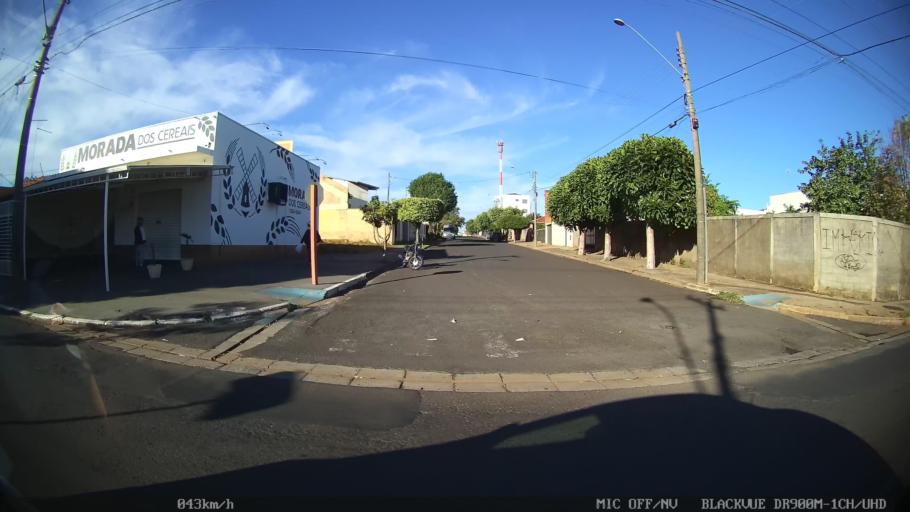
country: BR
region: Sao Paulo
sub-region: Araraquara
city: Araraquara
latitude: -21.7593
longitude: -48.1633
